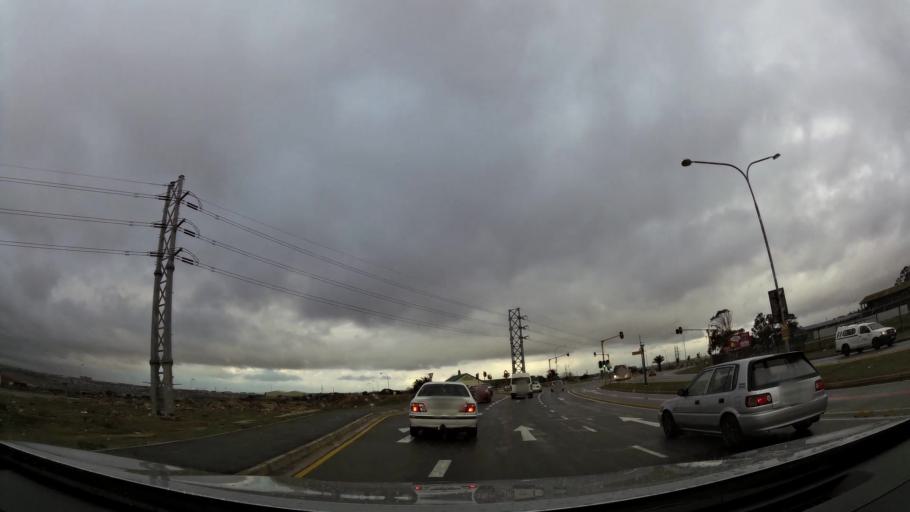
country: ZA
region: Eastern Cape
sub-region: Nelson Mandela Bay Metropolitan Municipality
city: Port Elizabeth
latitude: -33.8958
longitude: 25.5389
